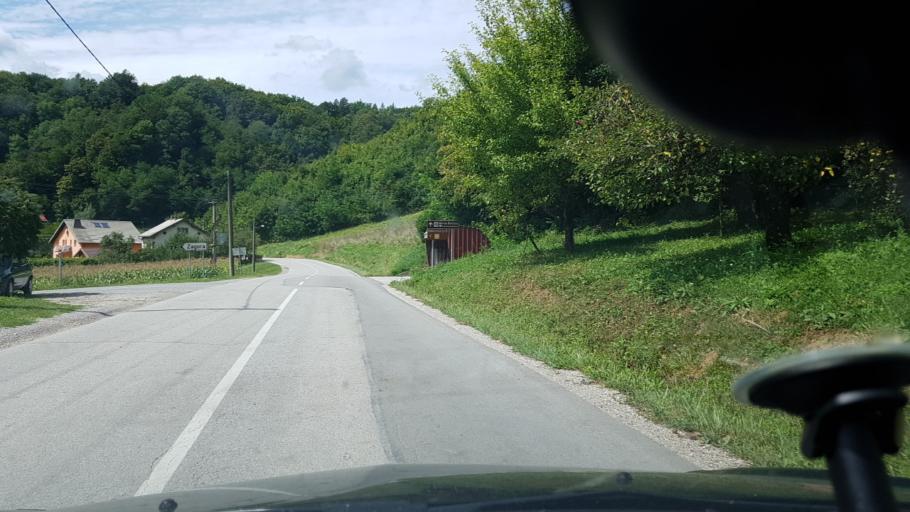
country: HR
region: Krapinsko-Zagorska
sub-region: Grad Krapina
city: Krapina
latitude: 46.1966
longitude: 15.8712
